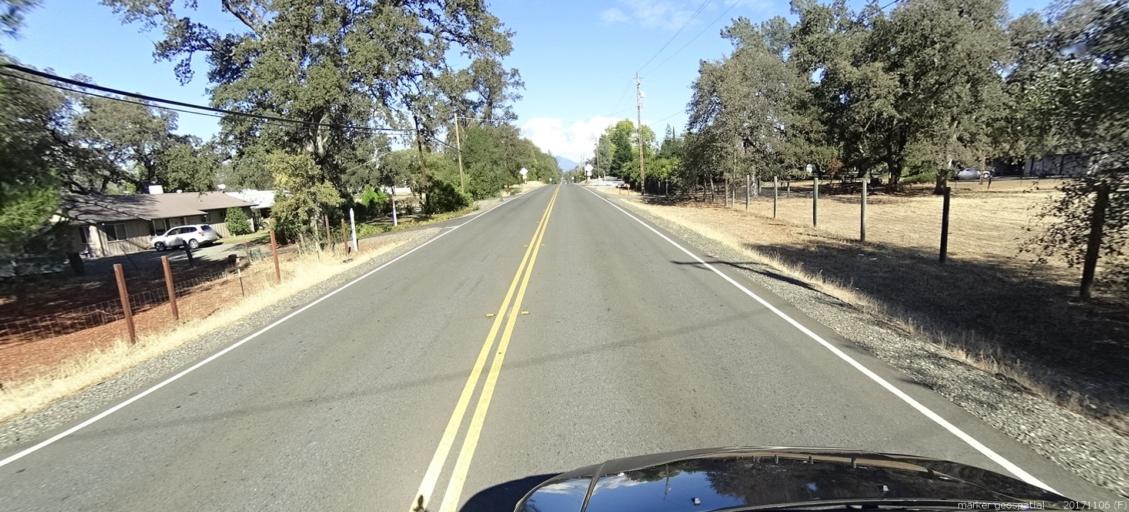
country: US
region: California
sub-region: Shasta County
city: Palo Cedro
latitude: 40.5738
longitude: -122.2387
